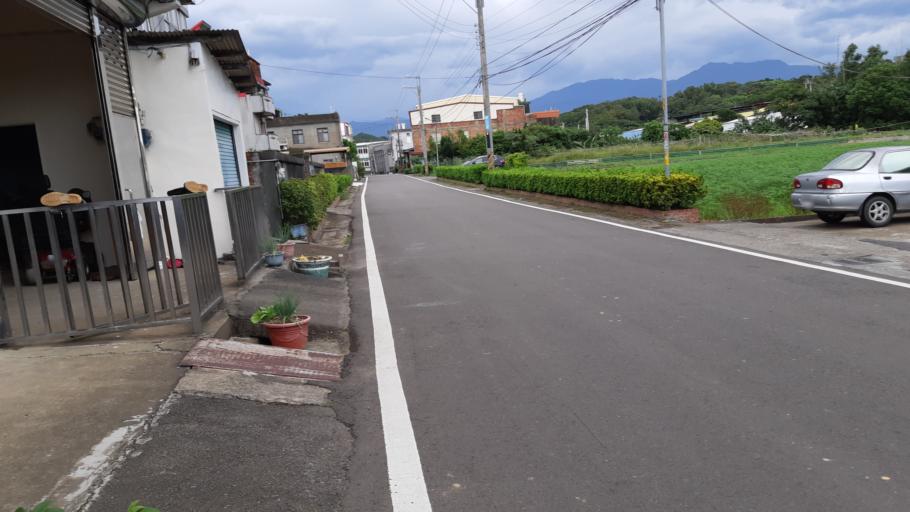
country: TW
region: Taiwan
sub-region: Miaoli
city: Miaoli
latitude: 24.6592
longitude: 120.8851
